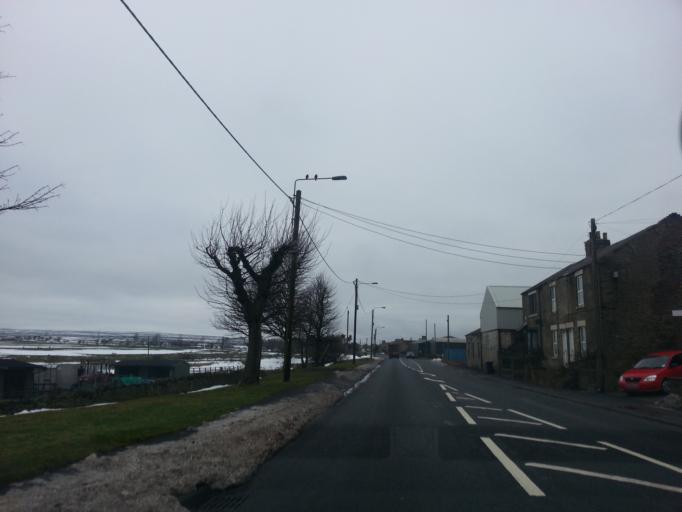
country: GB
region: England
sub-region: County Durham
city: Tow Law
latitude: 54.7513
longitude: -1.8230
